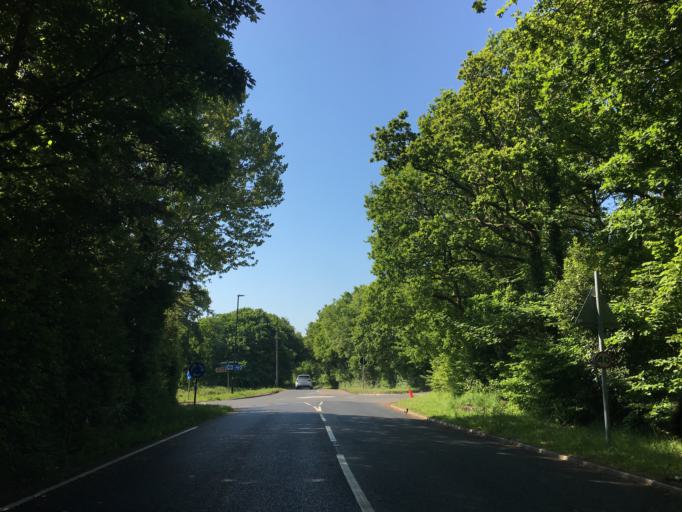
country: GB
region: England
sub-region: Isle of Wight
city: Ryde
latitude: 50.7115
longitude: -1.1654
